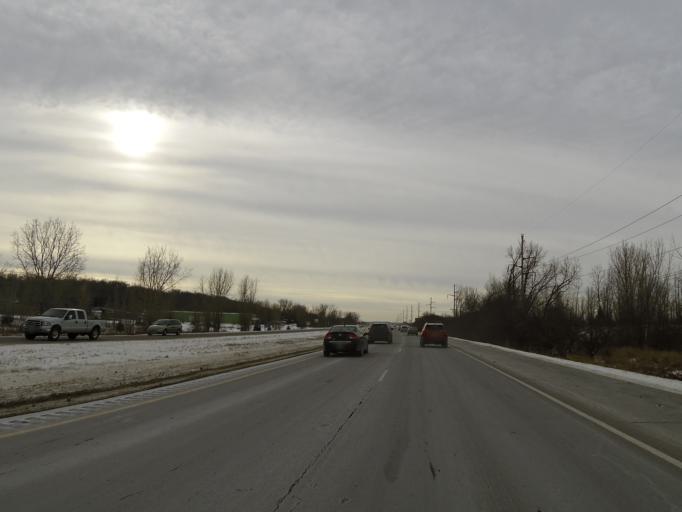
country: US
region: Minnesota
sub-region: Carver County
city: Chaska
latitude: 44.7535
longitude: -93.5862
